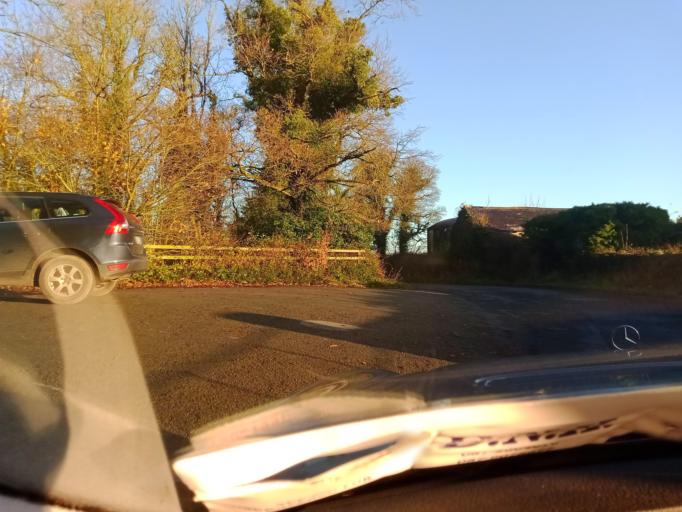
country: IE
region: Leinster
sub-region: Kilkenny
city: Callan
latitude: 52.5314
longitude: -7.4473
